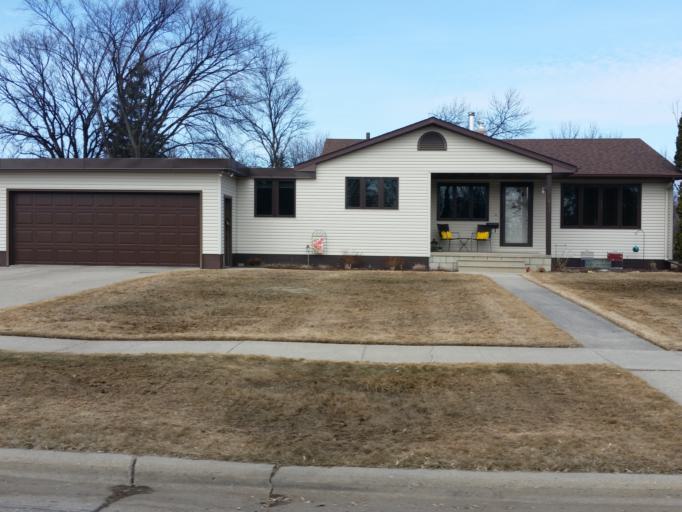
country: US
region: North Dakota
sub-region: Walsh County
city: Grafton
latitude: 48.4081
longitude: -97.4178
